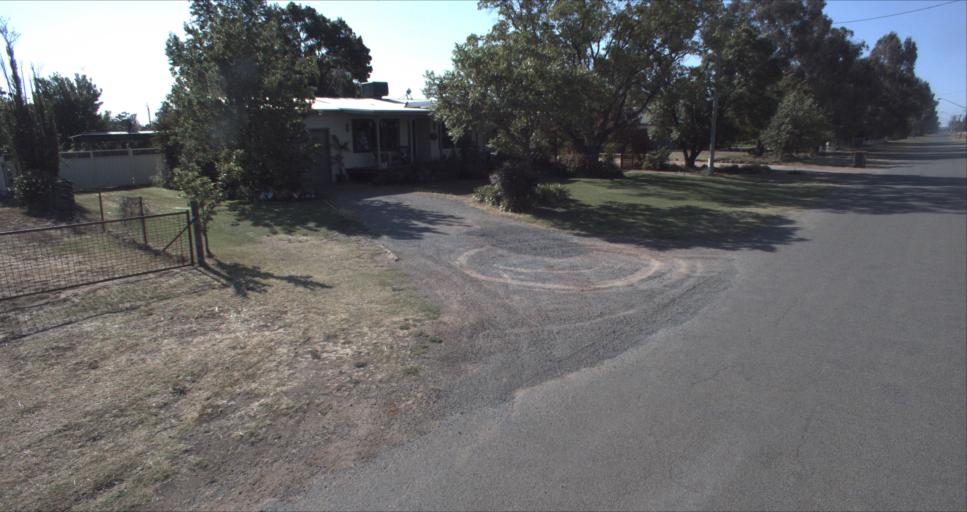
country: AU
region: New South Wales
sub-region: Leeton
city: Leeton
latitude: -34.5479
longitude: 146.4143
